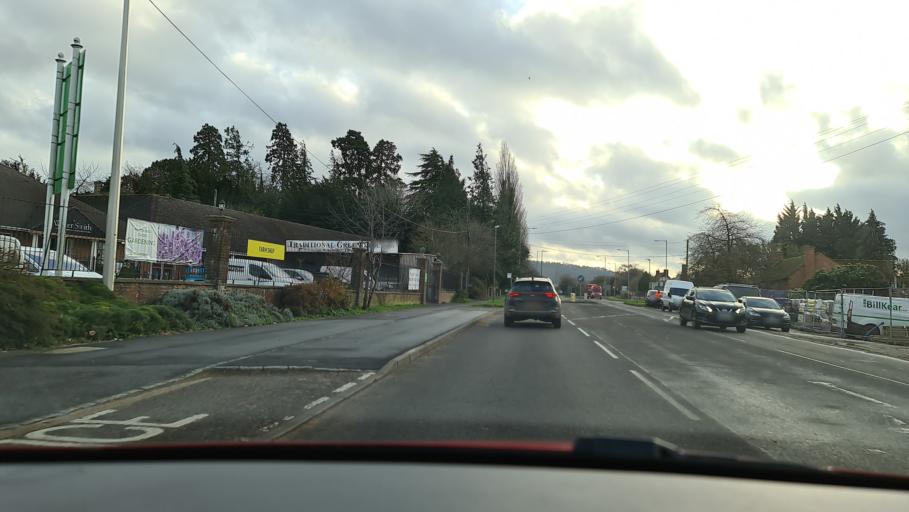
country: GB
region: England
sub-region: Buckinghamshire
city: Weston Turville
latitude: 51.7756
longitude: -0.7572
